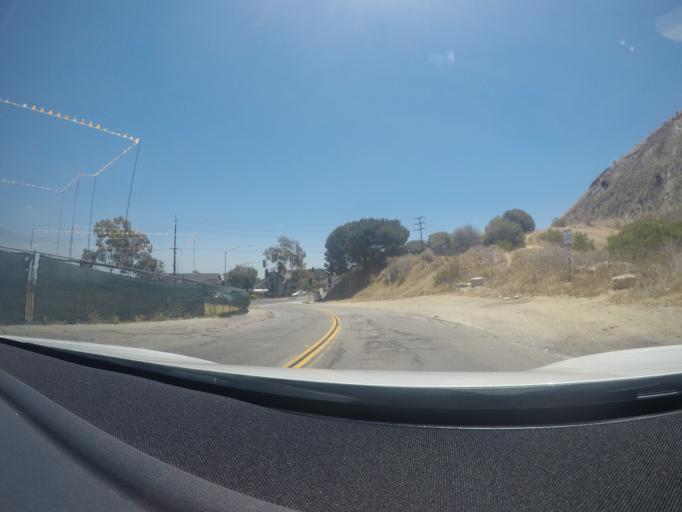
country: US
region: California
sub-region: Los Angeles County
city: Rolling Hills Estates
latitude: 33.7985
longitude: -118.3517
